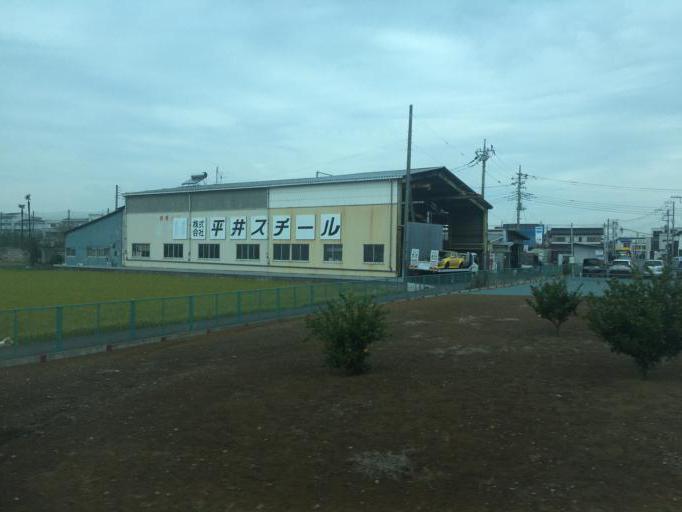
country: JP
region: Saitama
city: Kamifukuoka
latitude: 35.9038
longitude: 139.5251
